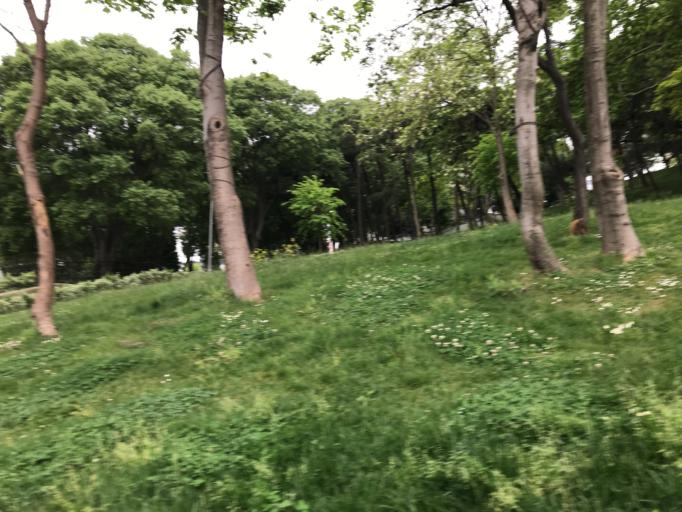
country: TR
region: Istanbul
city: Sisli
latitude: 41.0380
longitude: 28.9943
